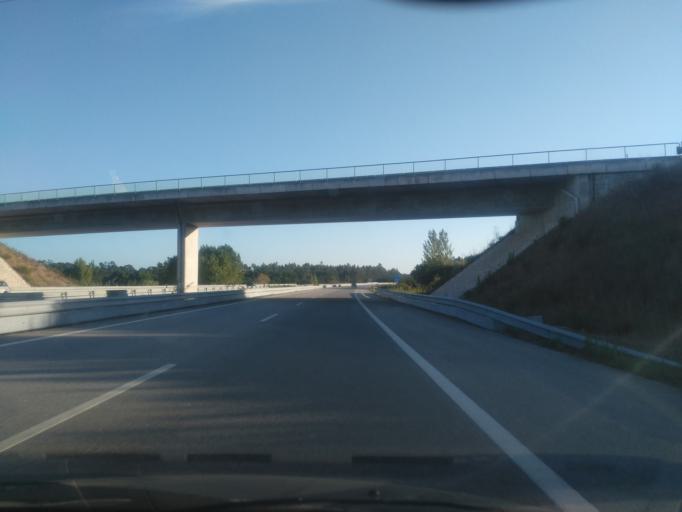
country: PT
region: Coimbra
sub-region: Figueira da Foz
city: Alhadas
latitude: 40.2355
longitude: -8.7855
